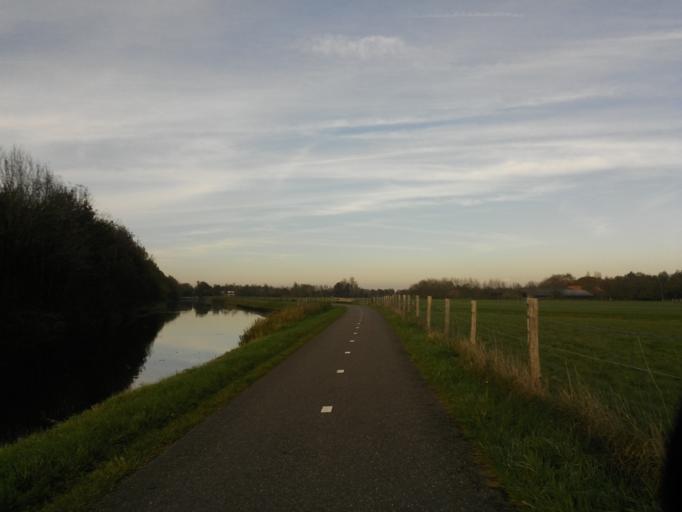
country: NL
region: Utrecht
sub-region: Gemeente Leusden
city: Leusden
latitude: 52.1226
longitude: 5.4457
